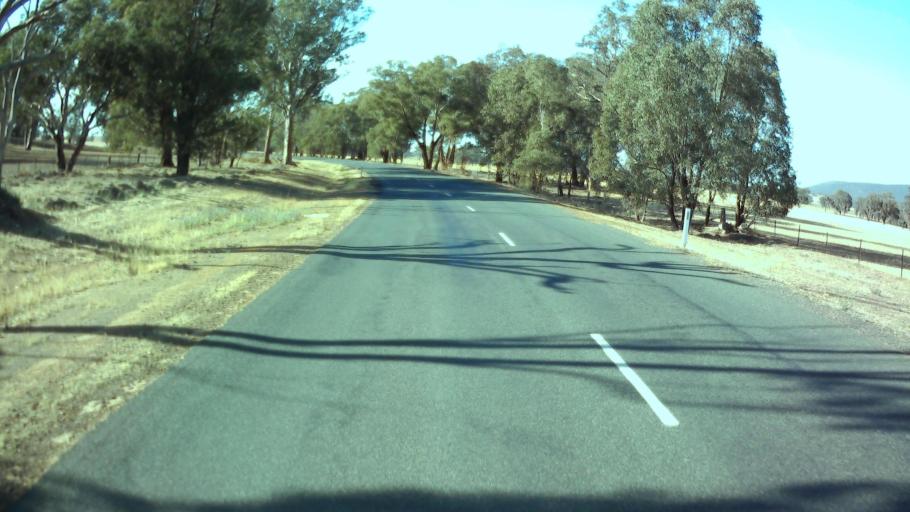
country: AU
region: New South Wales
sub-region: Weddin
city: Grenfell
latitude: -33.9436
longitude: 148.1356
